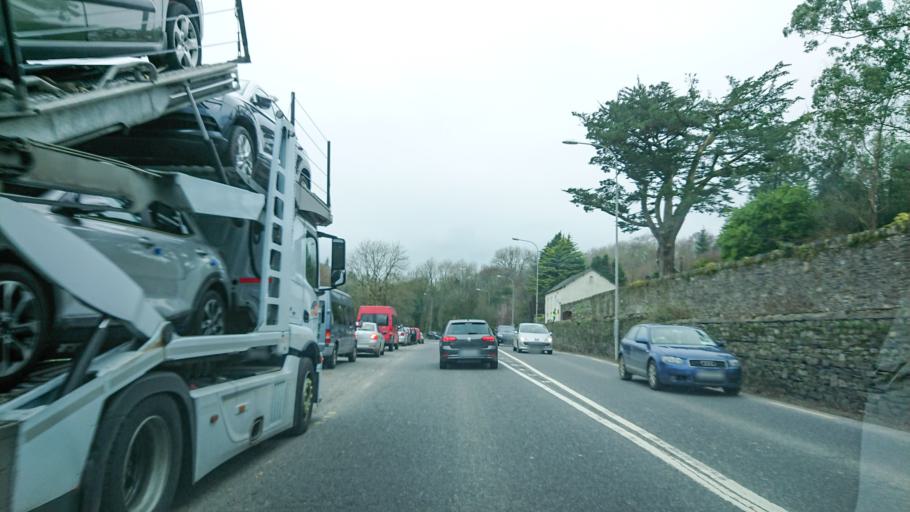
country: IE
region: Munster
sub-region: County Cork
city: Bandon
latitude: 51.7654
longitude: -8.6622
